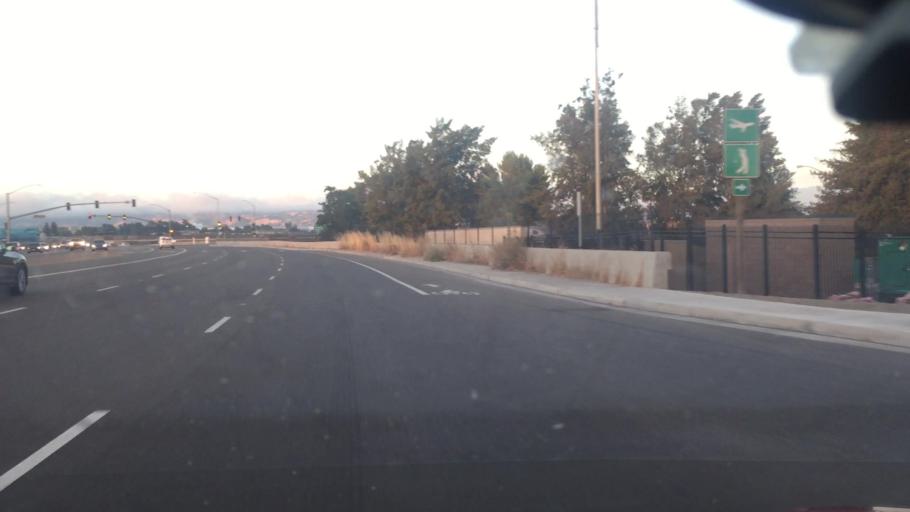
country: US
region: California
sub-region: Alameda County
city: Livermore
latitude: 37.6981
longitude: -121.8049
